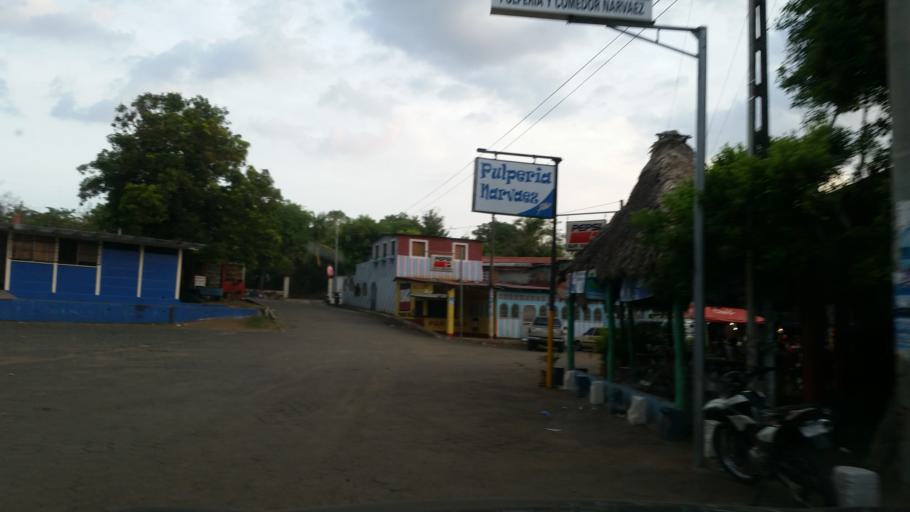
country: NI
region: Managua
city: Masachapa
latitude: 11.7714
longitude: -86.5045
